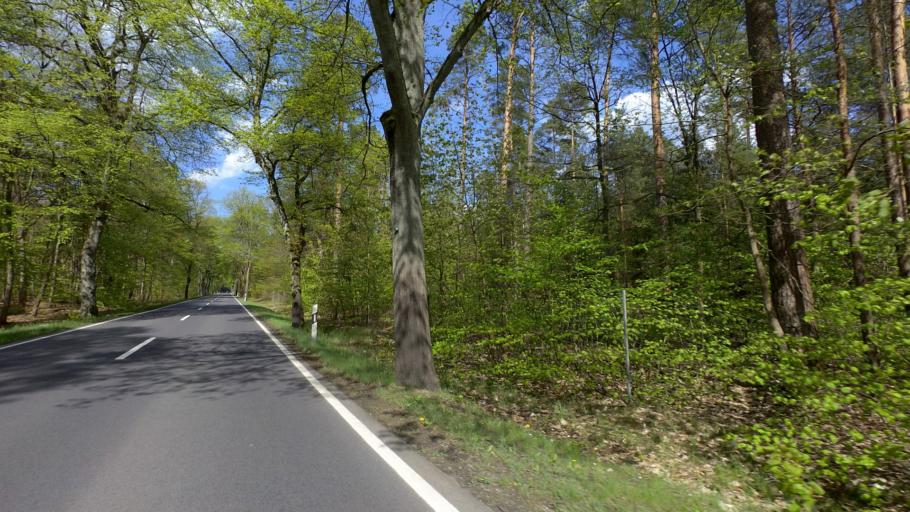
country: DE
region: Brandenburg
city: Friedrichswalde
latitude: 53.0127
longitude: 13.6014
